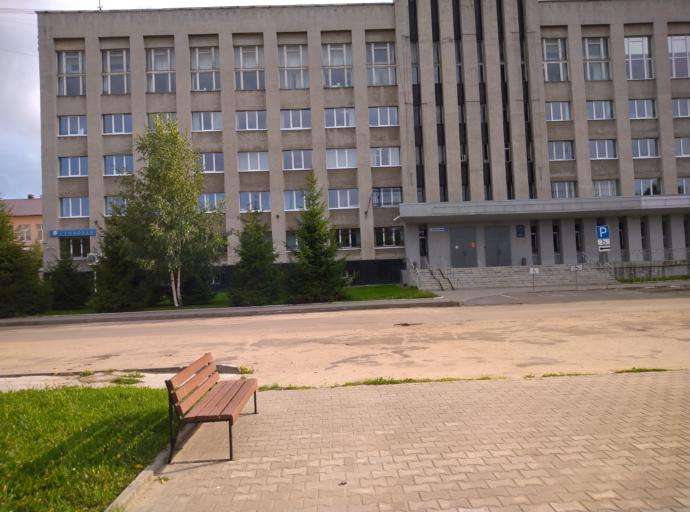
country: RU
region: Kostroma
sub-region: Kostromskoy Rayon
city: Kostroma
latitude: 57.7588
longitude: 40.9628
